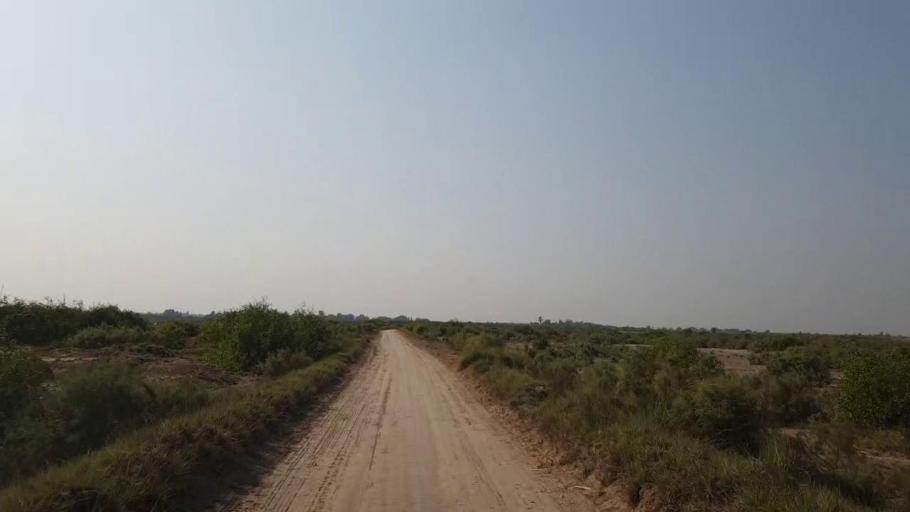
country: PK
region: Sindh
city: Bulri
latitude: 24.9465
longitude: 68.3821
